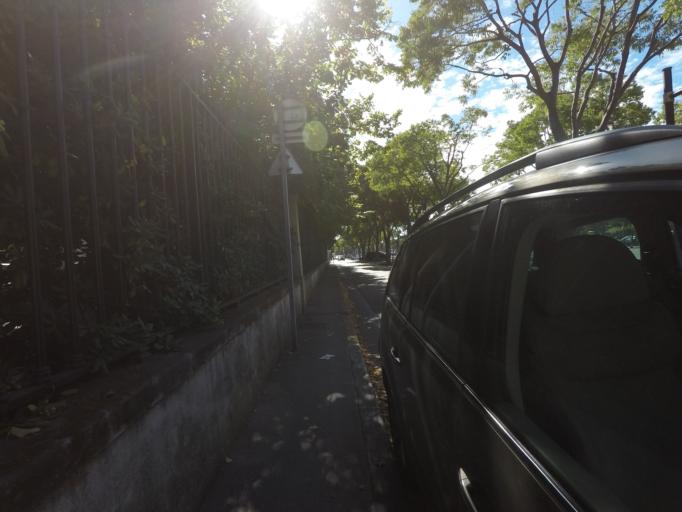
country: FR
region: Provence-Alpes-Cote d'Azur
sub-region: Departement des Bouches-du-Rhone
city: Marseille 08
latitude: 43.2678
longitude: 5.3843
